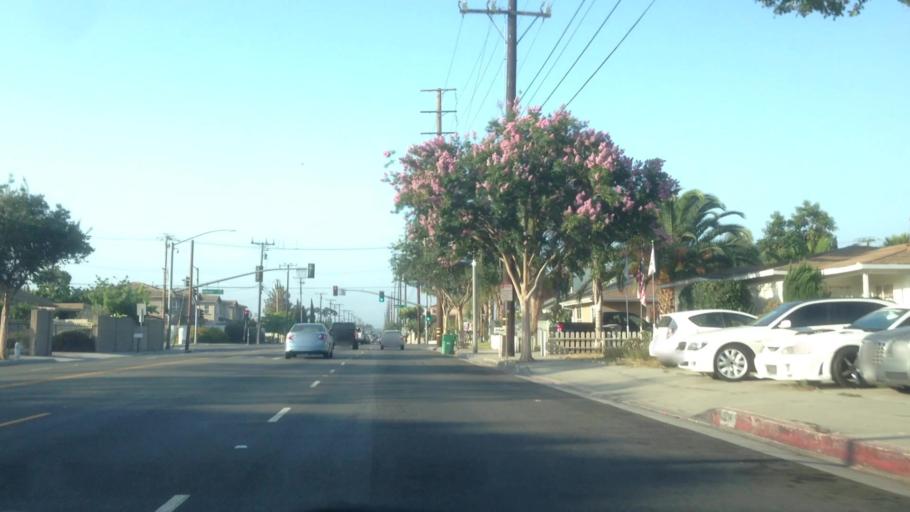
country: US
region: California
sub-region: Orange County
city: Fountain Valley
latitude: 33.7320
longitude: -117.9287
